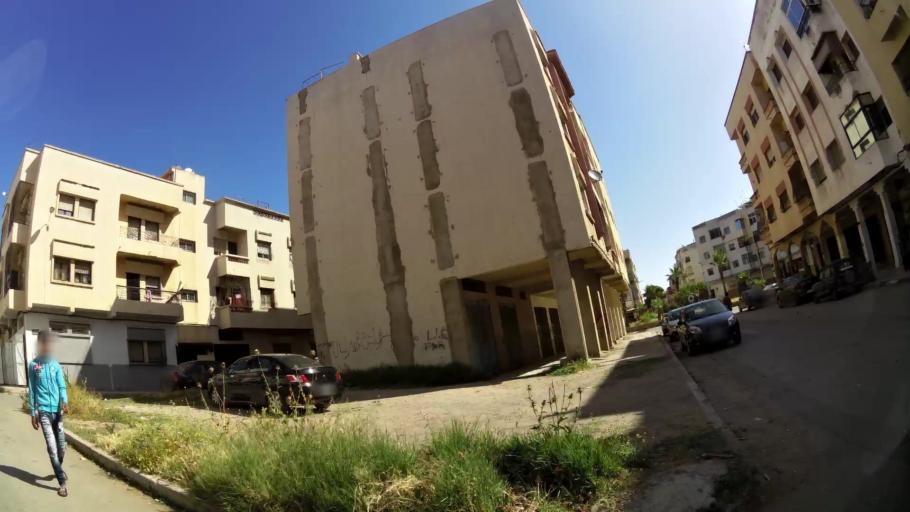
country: MA
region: Rabat-Sale-Zemmour-Zaer
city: Sale
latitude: 34.0652
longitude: -6.7996
